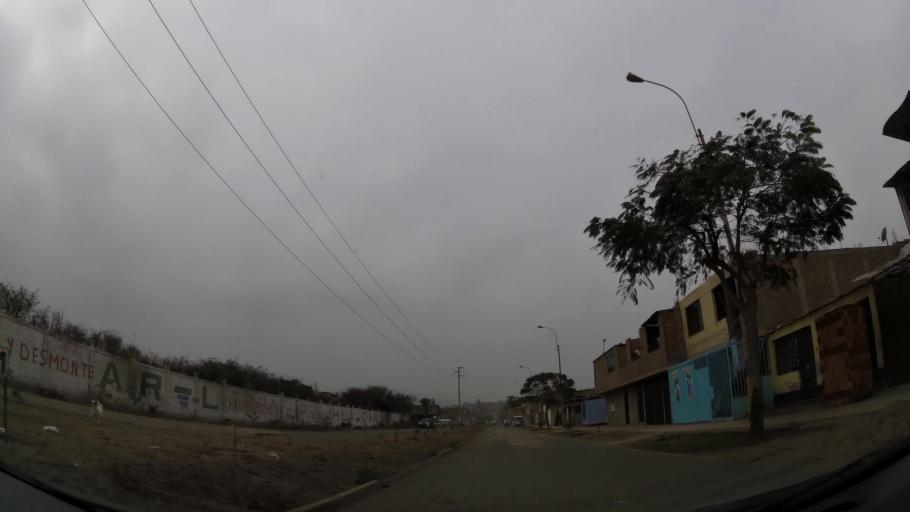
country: PE
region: Lima
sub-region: Lima
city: Surco
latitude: -12.2371
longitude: -76.9249
